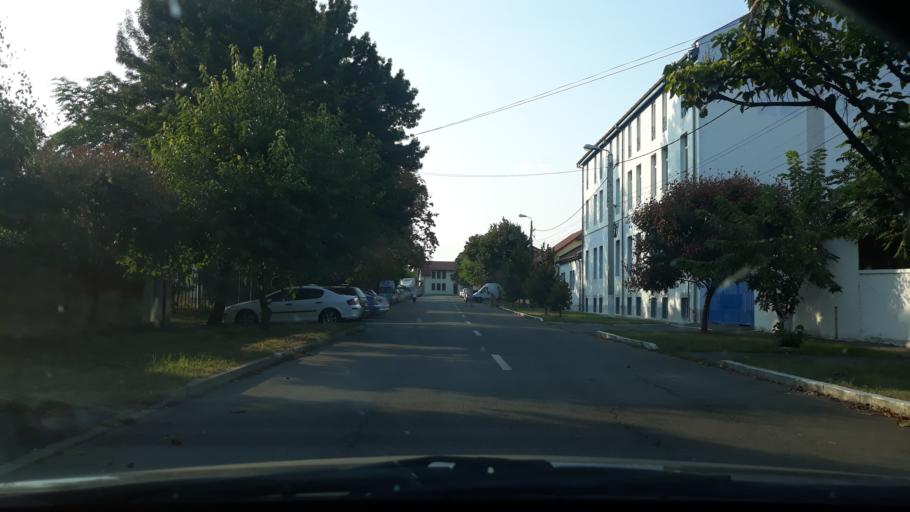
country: RO
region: Bihor
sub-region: Comuna Biharea
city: Oradea
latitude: 47.0510
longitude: 21.9469
